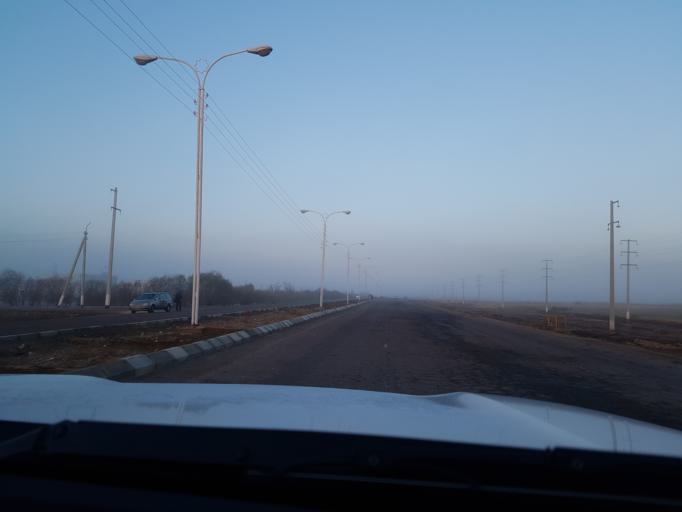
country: TM
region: Dasoguz
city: Koeneuergench
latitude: 41.7428
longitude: 58.7009
